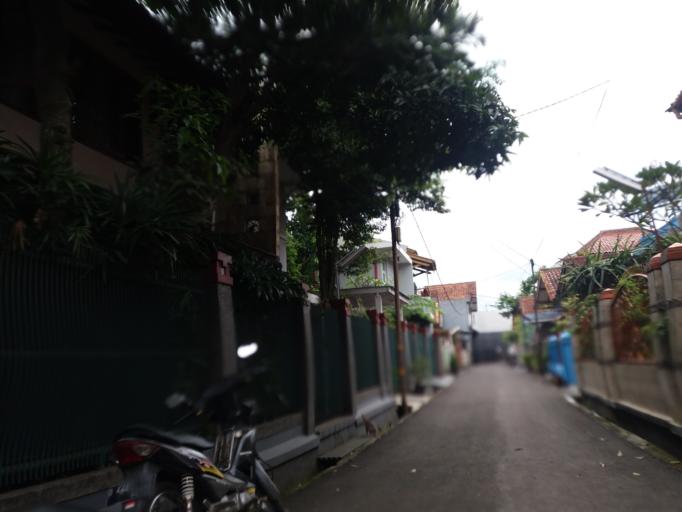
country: ID
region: West Java
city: Bandung
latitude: -6.9213
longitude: 107.6542
